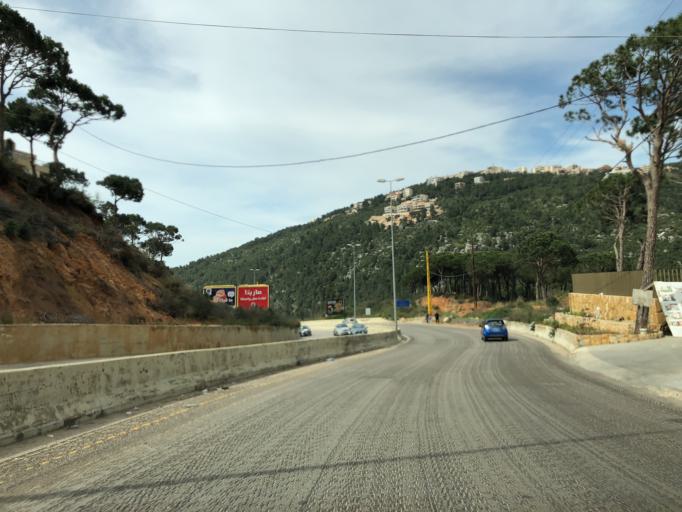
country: LB
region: Mont-Liban
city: Bhamdoun el Mhatta
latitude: 33.8903
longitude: 35.6613
